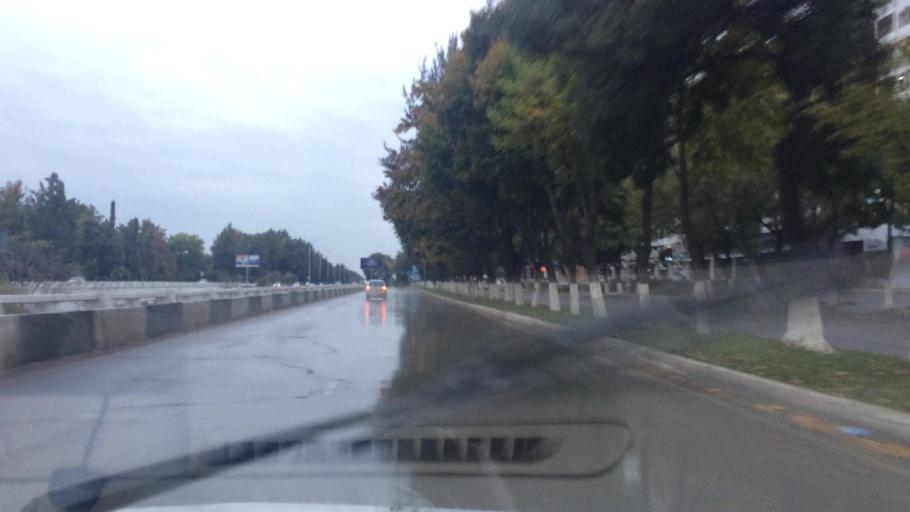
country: UZ
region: Toshkent Shahri
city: Tashkent
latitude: 41.3100
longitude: 69.2396
